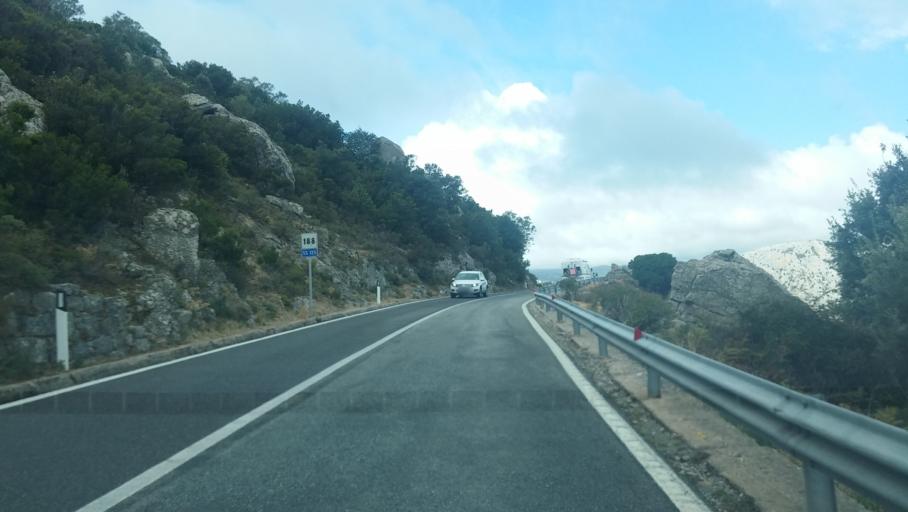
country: IT
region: Sardinia
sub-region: Provincia di Ogliastra
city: Urzulei
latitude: 40.1791
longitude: 9.5315
